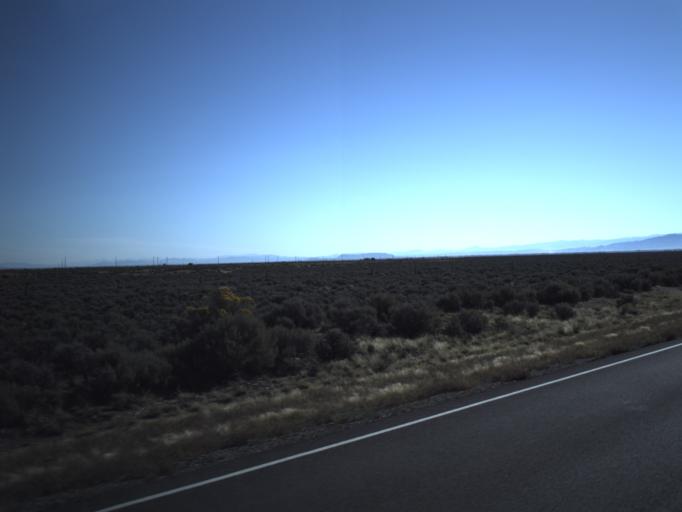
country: US
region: Utah
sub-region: Washington County
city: Enterprise
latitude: 37.7919
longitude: -113.8917
